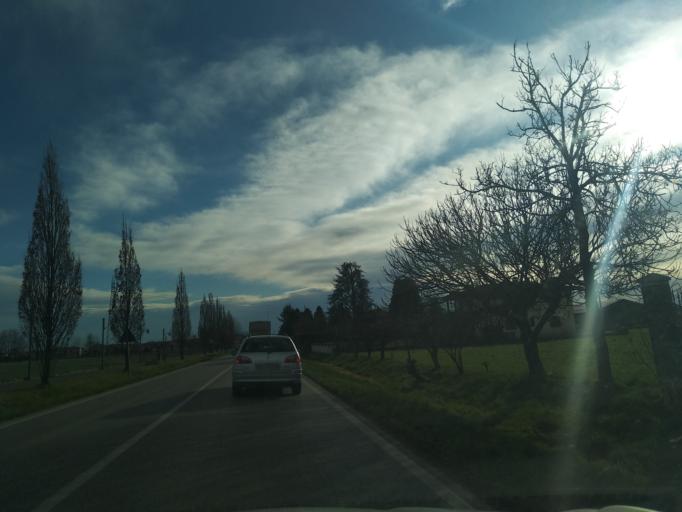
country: IT
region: Veneto
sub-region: Provincia di Vicenza
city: Bressanvido
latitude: 45.6400
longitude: 11.6280
